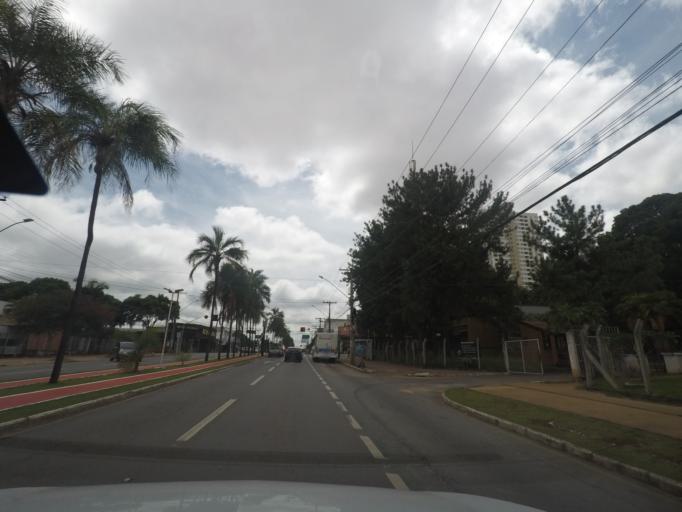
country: BR
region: Goias
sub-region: Goiania
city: Goiania
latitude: -16.6763
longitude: -49.2413
